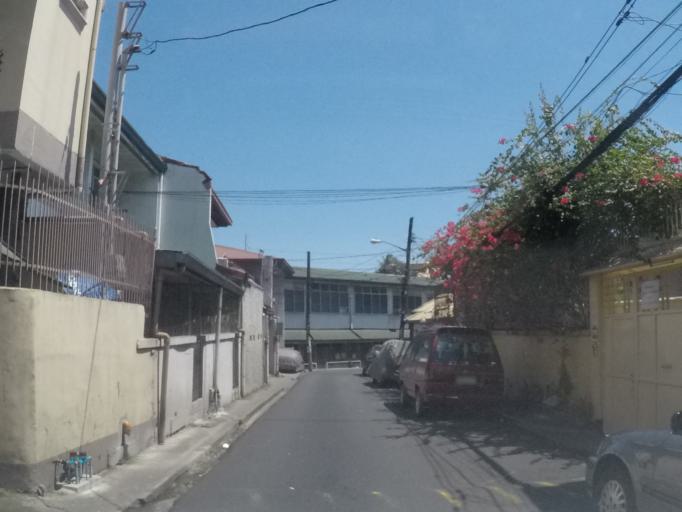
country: PH
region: Metro Manila
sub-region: San Juan
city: San Juan
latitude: 14.6055
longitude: 121.0250
